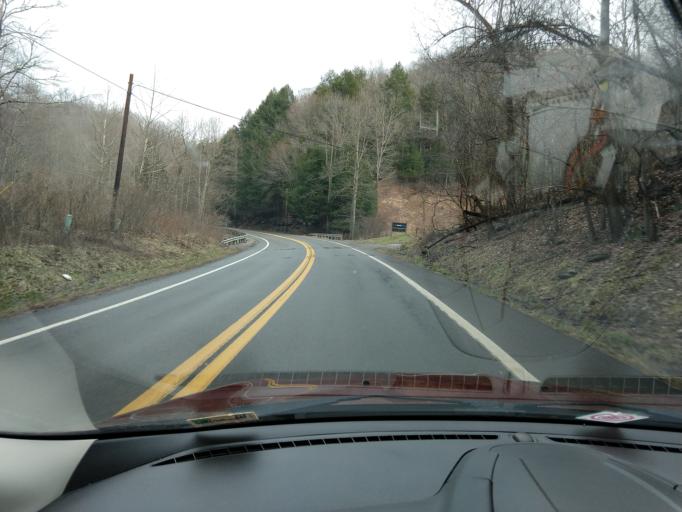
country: US
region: West Virginia
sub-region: Wyoming County
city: Pineville
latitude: 37.5504
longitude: -81.5721
